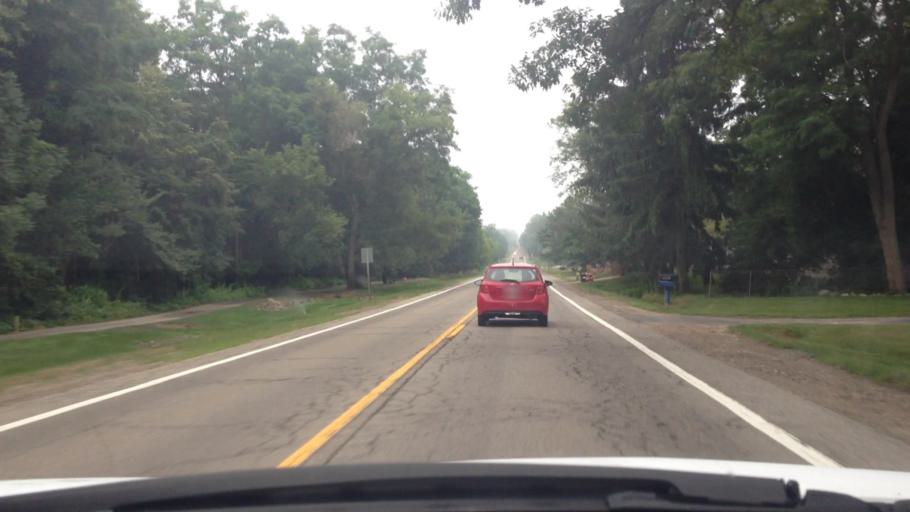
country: US
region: Michigan
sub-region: Oakland County
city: Clarkston
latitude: 42.7411
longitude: -83.3503
